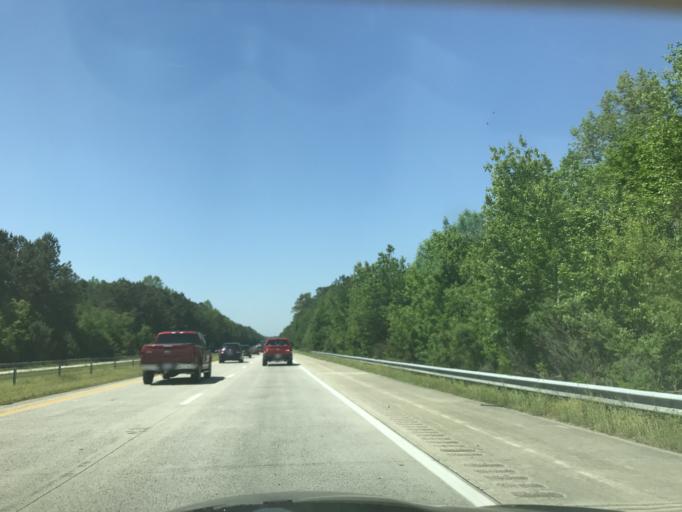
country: US
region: North Carolina
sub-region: Johnston County
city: Benson
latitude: 35.4796
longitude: -78.5504
